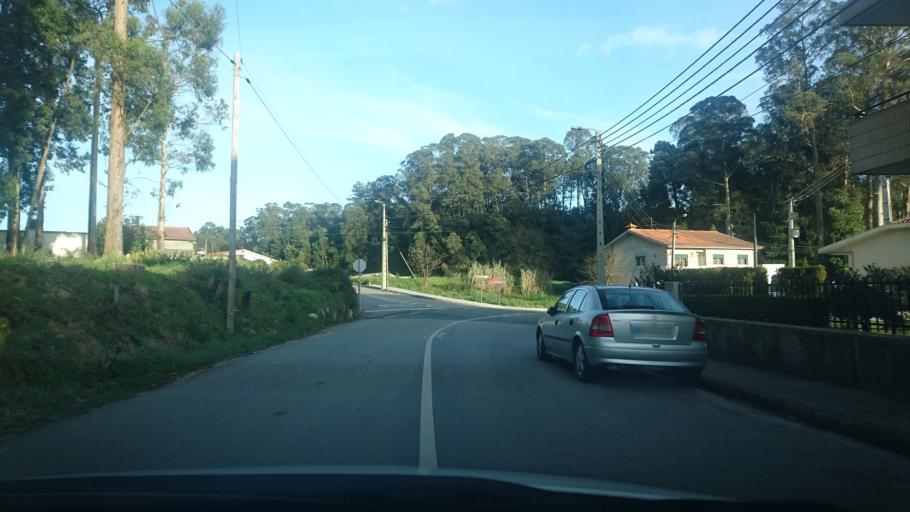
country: PT
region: Aveiro
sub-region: Santa Maria da Feira
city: Nogueira da Regedoura
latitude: 40.9994
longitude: -8.5975
